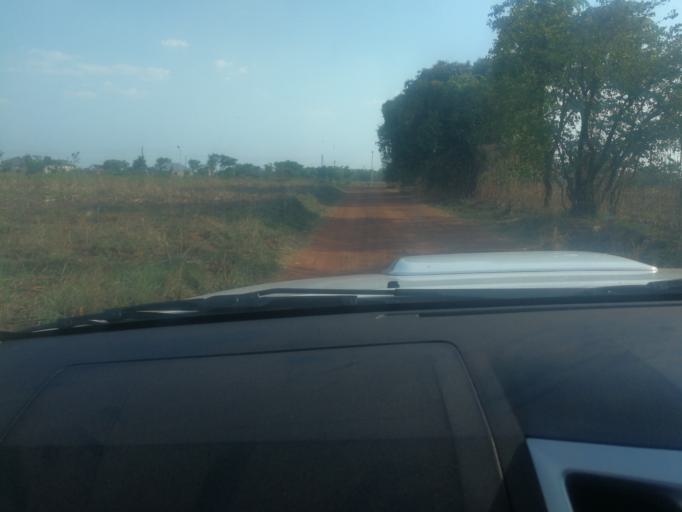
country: ZM
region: Northern
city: Kasama
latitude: -10.2170
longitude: 31.1411
